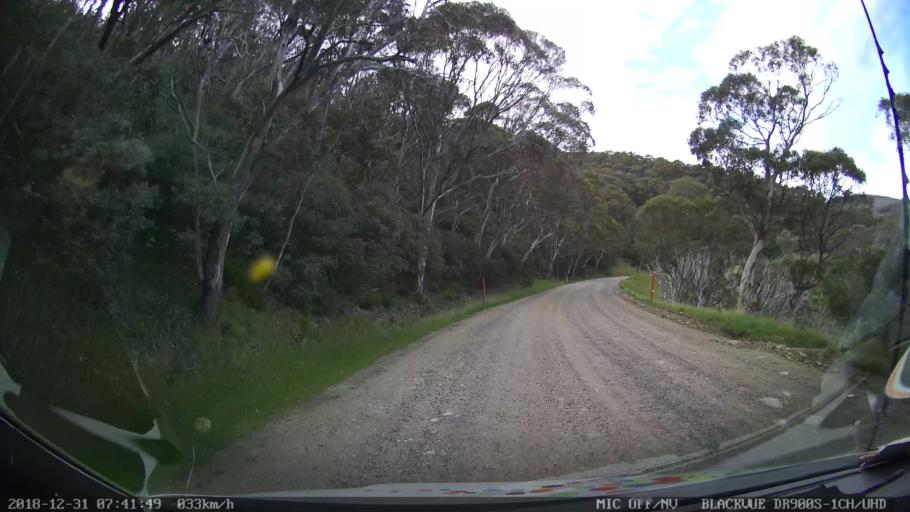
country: AU
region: New South Wales
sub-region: Snowy River
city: Jindabyne
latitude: -36.3550
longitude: 148.4117
